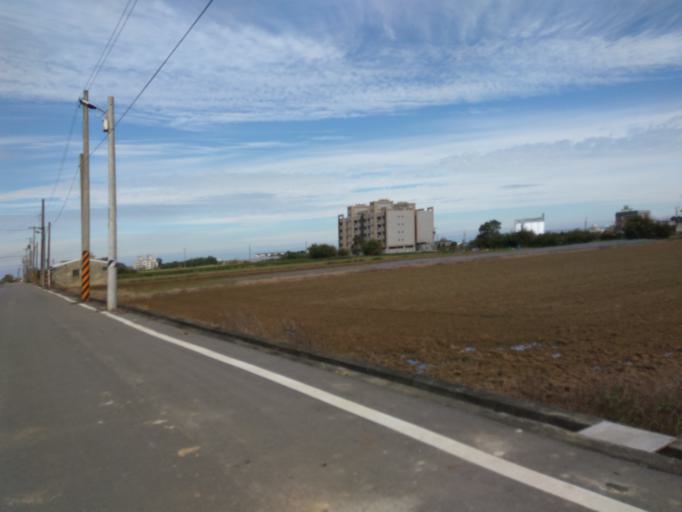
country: TW
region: Taiwan
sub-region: Hsinchu
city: Zhubei
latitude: 24.9882
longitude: 121.0926
